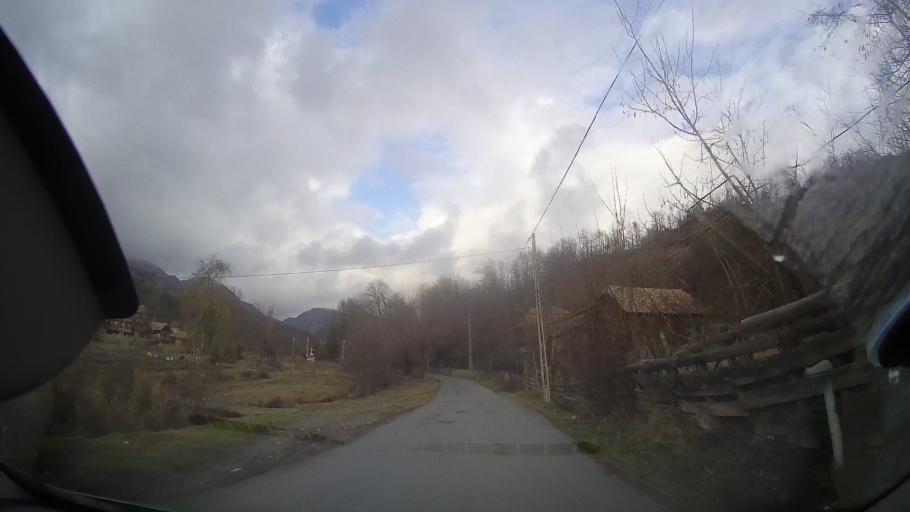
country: RO
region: Alba
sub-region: Comuna Ocolis
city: Ocolis
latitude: 46.4859
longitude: 23.4608
